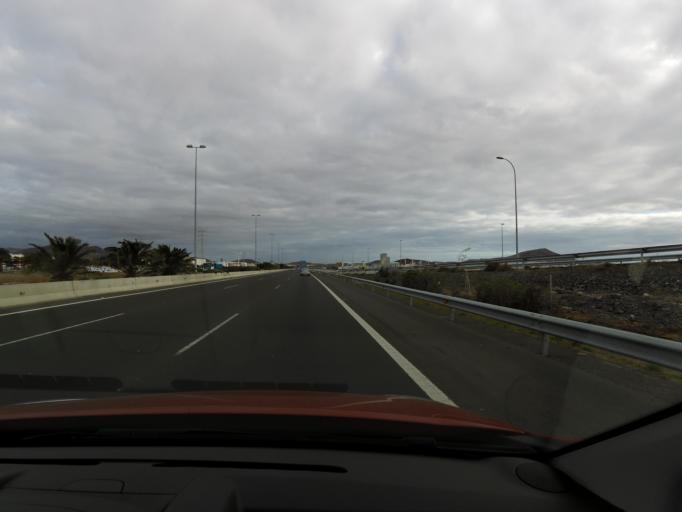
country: ES
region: Canary Islands
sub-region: Provincia de Las Palmas
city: Cruce de Arinaga
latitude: 27.8541
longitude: -15.4297
